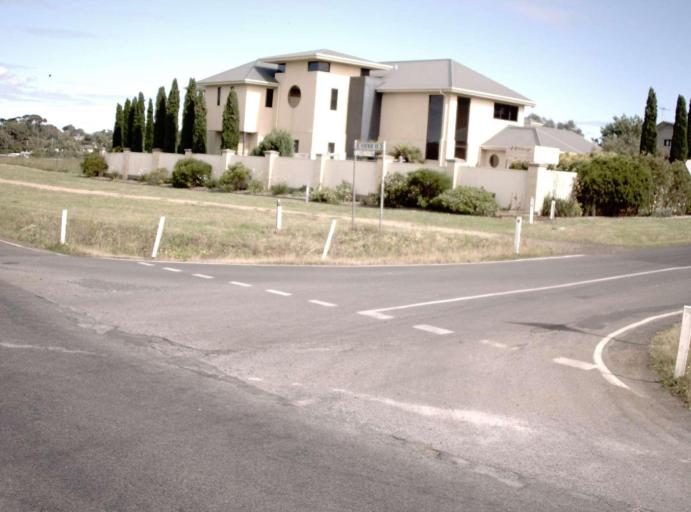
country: AU
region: Victoria
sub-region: Bass Coast
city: Phillip Island
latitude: -38.4636
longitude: 145.2015
